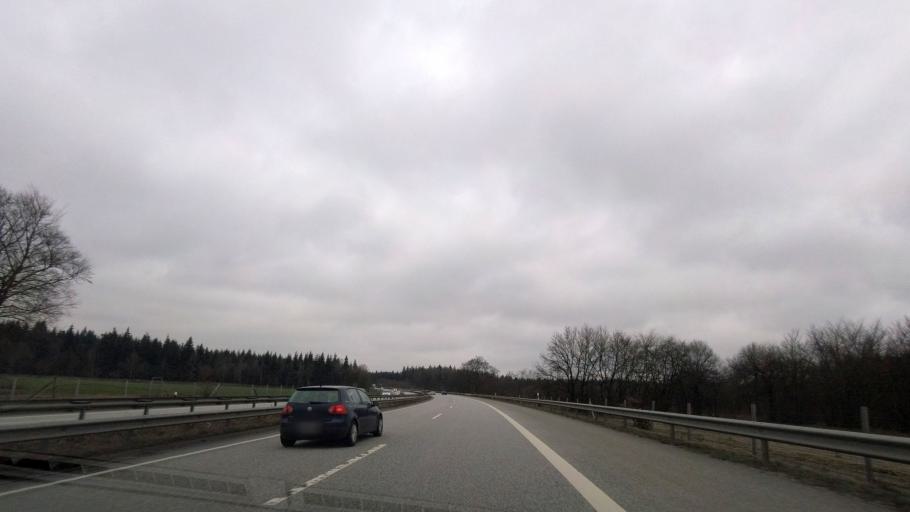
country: DE
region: Schleswig-Holstein
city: Daldorf
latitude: 54.0244
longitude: 10.2450
